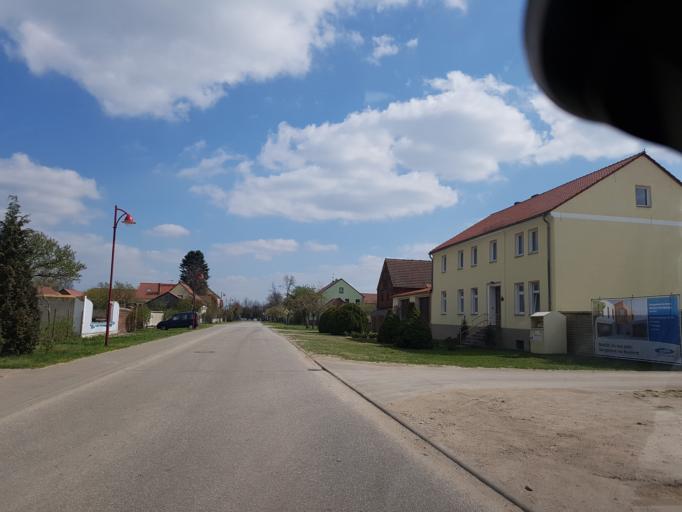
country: DE
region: Brandenburg
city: Bruck
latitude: 52.1784
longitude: 12.7680
